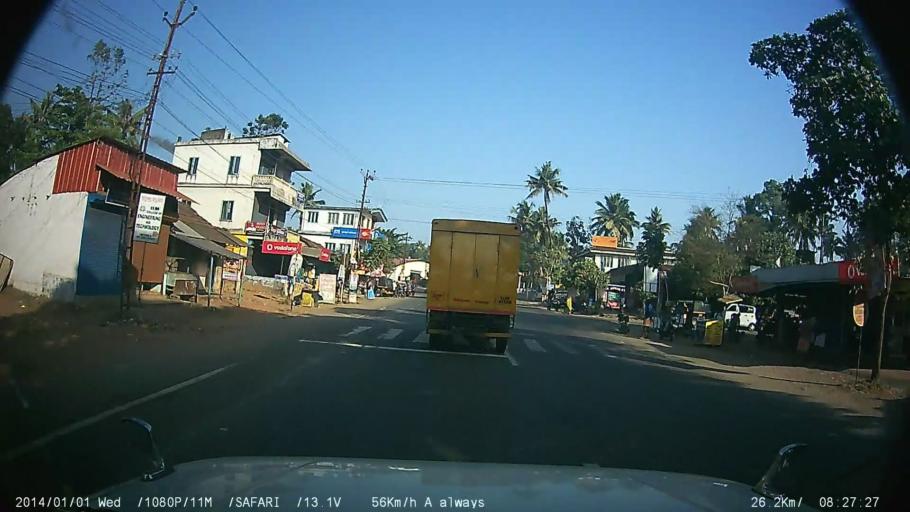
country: IN
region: Kerala
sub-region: Ernakulam
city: Perumbavoor
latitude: 10.0852
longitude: 76.5021
